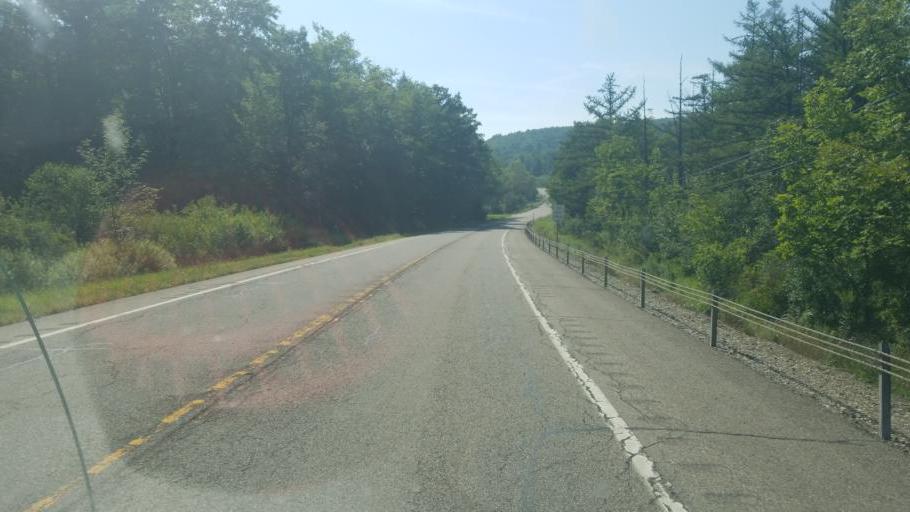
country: US
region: New York
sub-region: Allegany County
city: Wellsville
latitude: 42.1034
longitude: -78.0303
